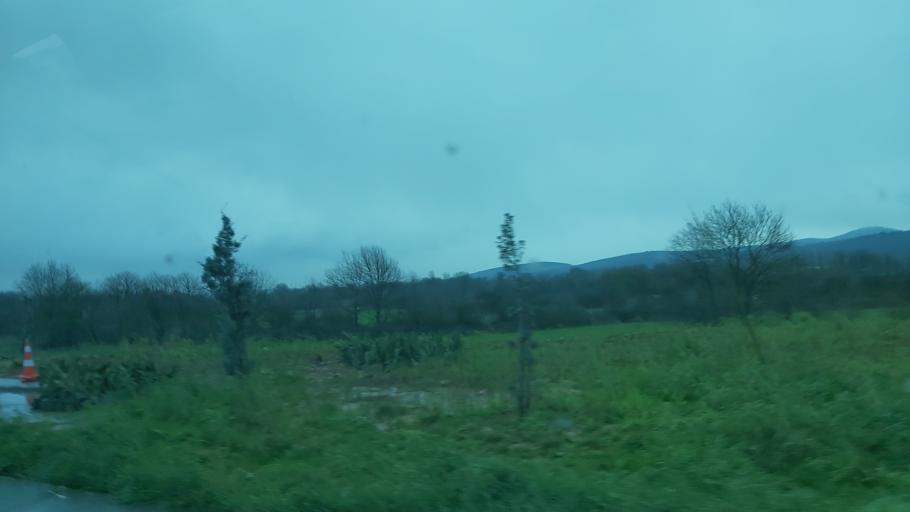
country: TR
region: Istanbul
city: Mahmut Sevket Pasa
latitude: 41.1147
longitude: 29.2977
